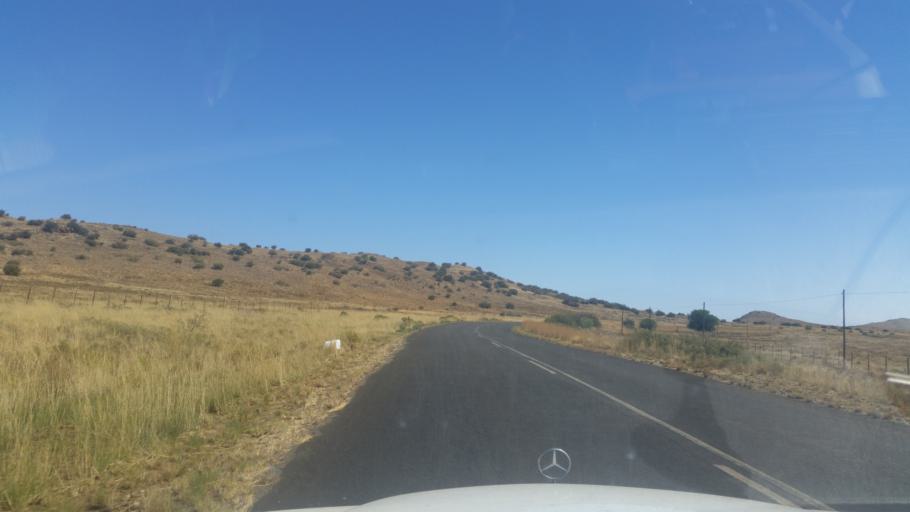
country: ZA
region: Eastern Cape
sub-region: Joe Gqabi District Municipality
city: Burgersdorp
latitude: -30.7410
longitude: 25.7564
